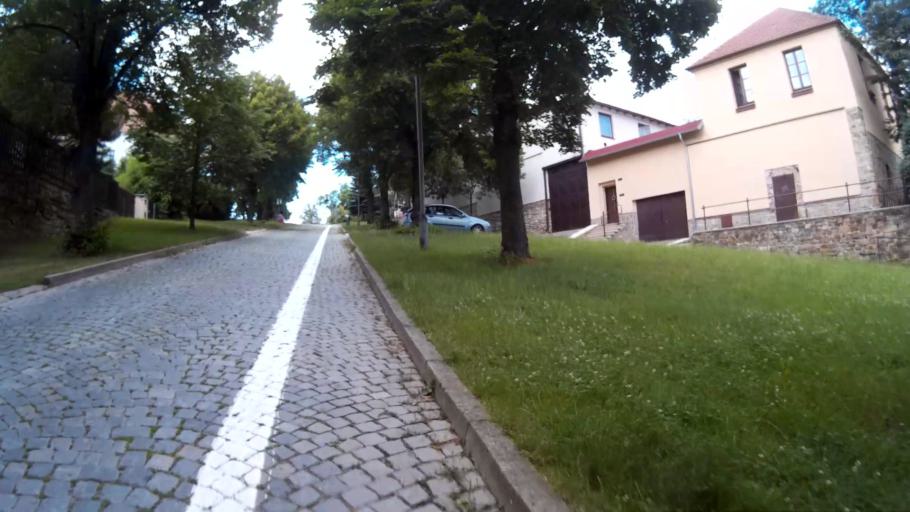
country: CZ
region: South Moravian
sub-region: Okres Brno-Venkov
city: Rosice
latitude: 49.1816
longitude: 16.3870
